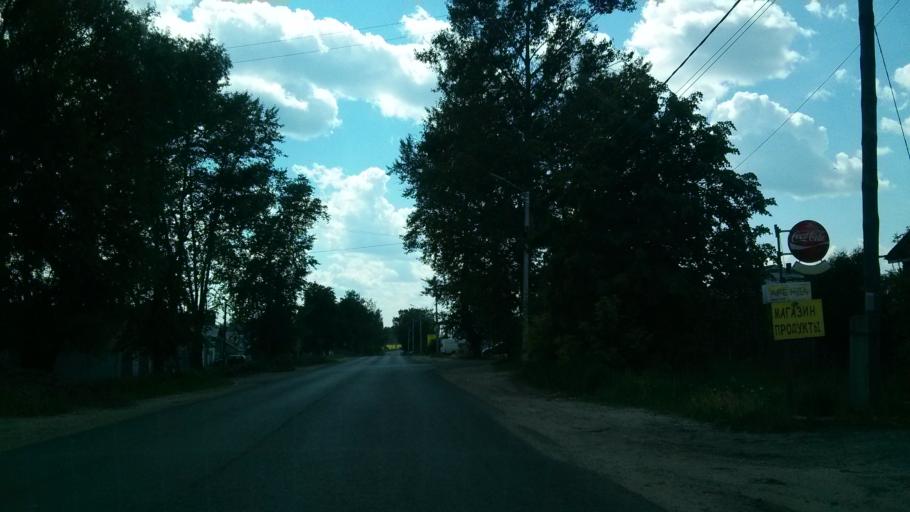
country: RU
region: Vladimir
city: Murom
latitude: 55.5319
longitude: 41.9646
